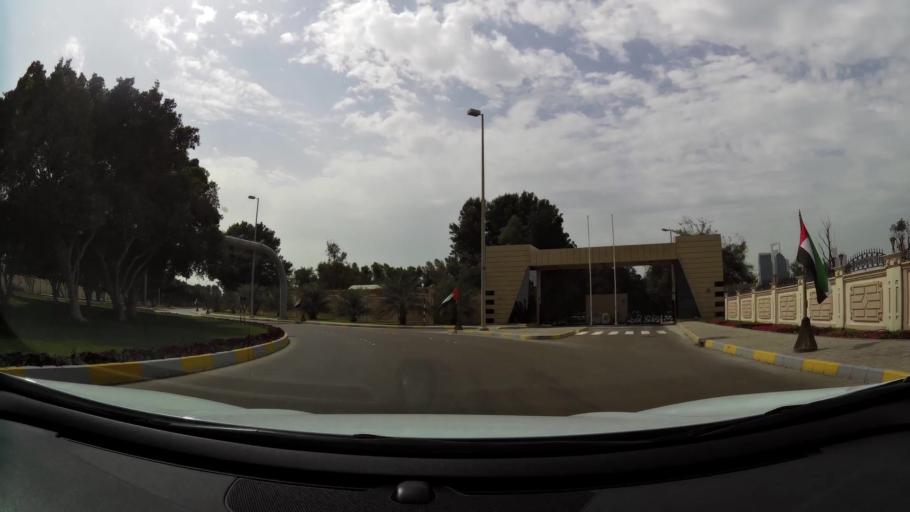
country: AE
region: Abu Dhabi
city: Abu Dhabi
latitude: 24.4499
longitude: 54.3477
